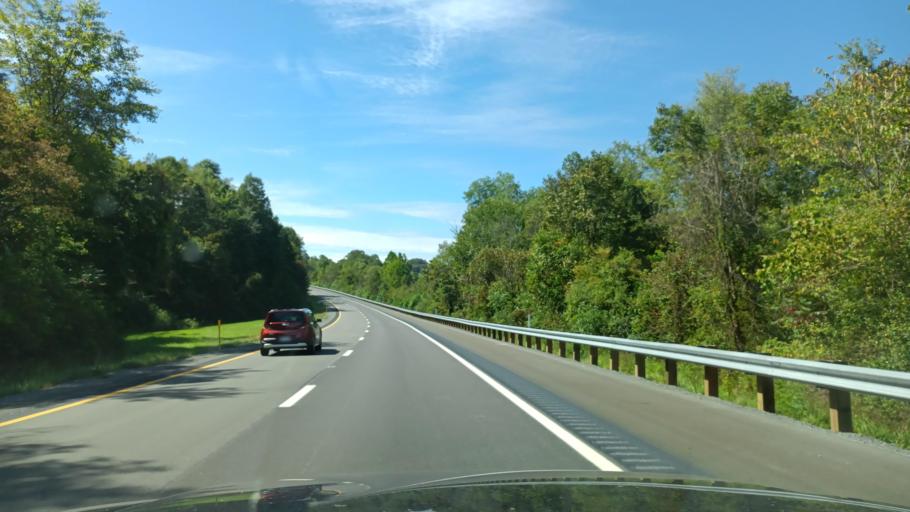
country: US
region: West Virginia
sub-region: Harrison County
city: Clarksburg
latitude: 39.2871
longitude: -80.4367
